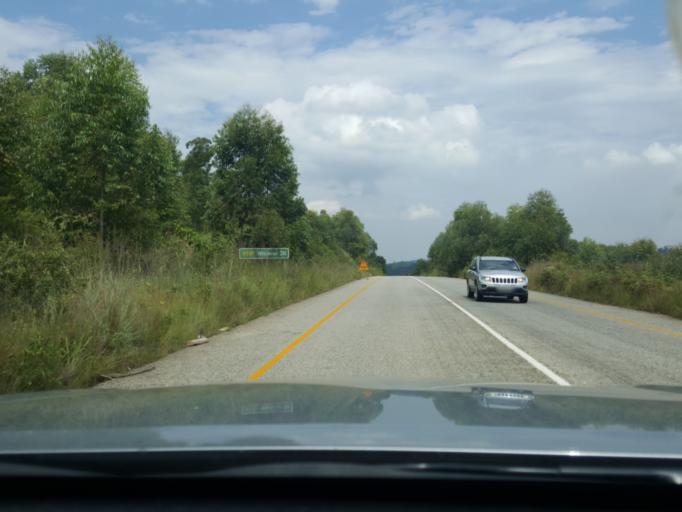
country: ZA
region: Mpumalanga
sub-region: Ehlanzeni District
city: White River
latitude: -25.1929
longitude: 30.9103
